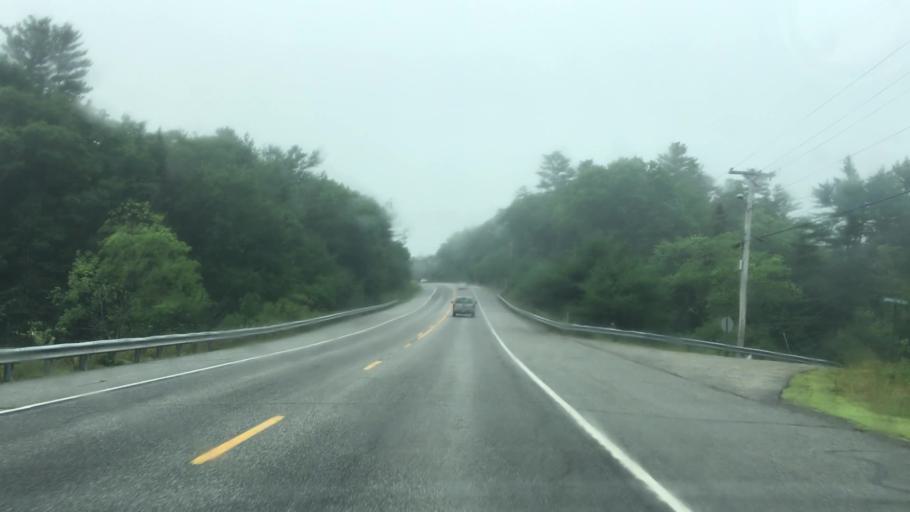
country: US
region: Maine
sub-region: Lincoln County
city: Edgecomb
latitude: 43.9408
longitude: -69.6261
